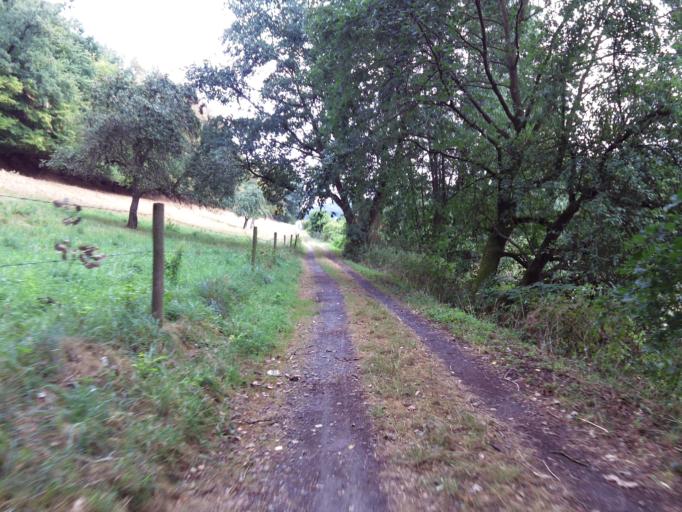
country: DE
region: Hesse
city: Reichelsheim
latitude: 49.7102
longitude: 8.8614
